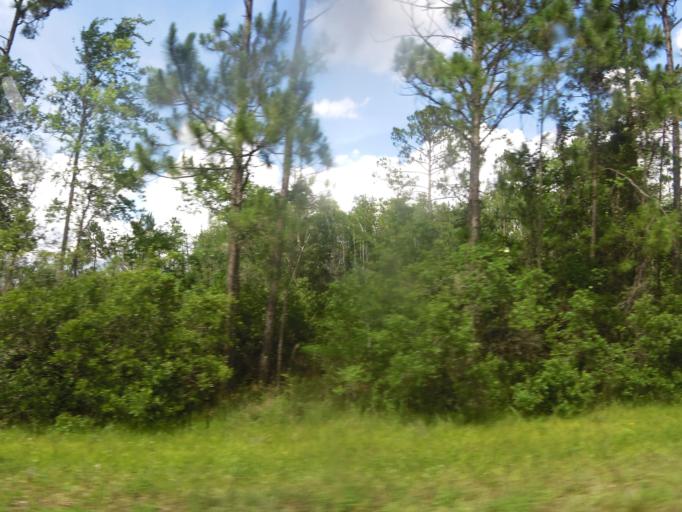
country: US
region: Florida
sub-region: Baker County
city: Macclenny
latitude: 30.2101
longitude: -82.0626
